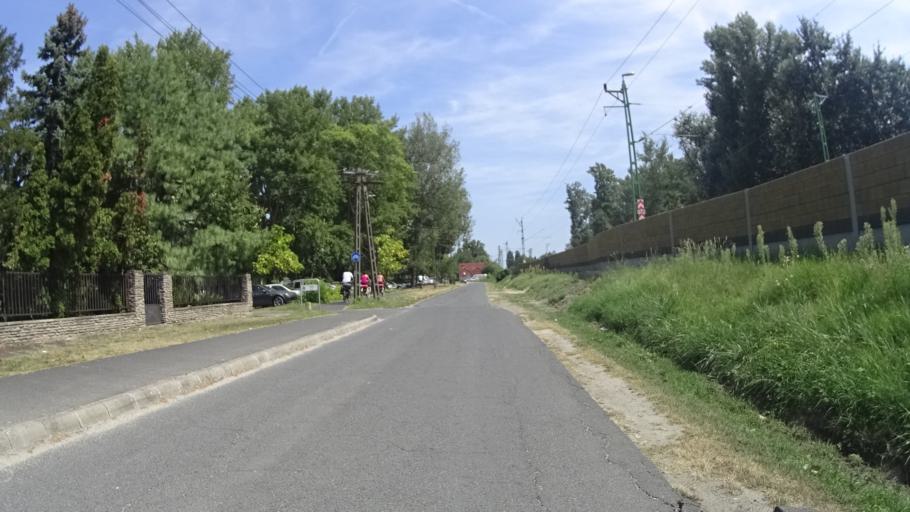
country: HU
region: Somogy
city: Fonyod
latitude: 46.7532
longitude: 17.5706
